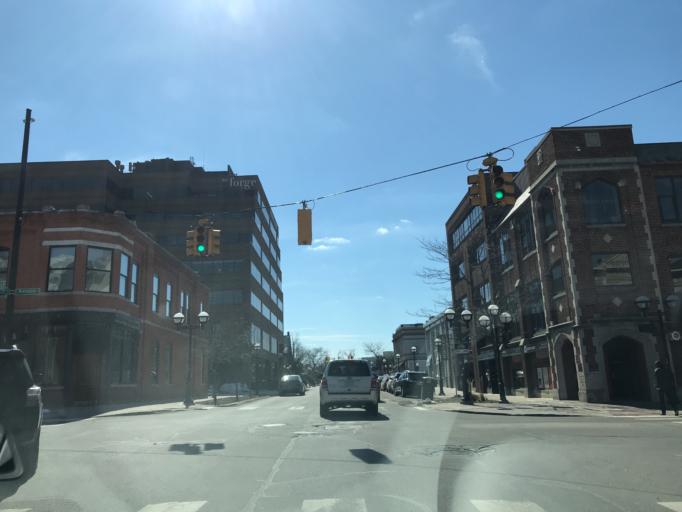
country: US
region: Michigan
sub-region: Washtenaw County
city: Ann Arbor
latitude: 42.2806
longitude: -83.7461
